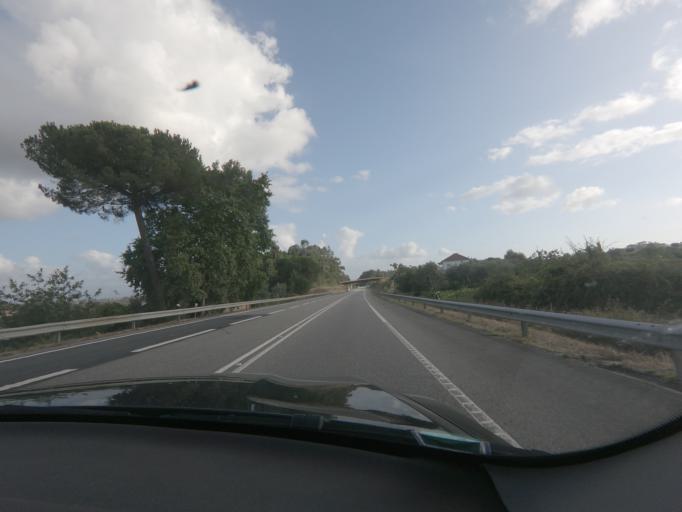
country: PT
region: Viseu
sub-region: Concelho de Tondela
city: Tondela
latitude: 40.5507
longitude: -8.0529
